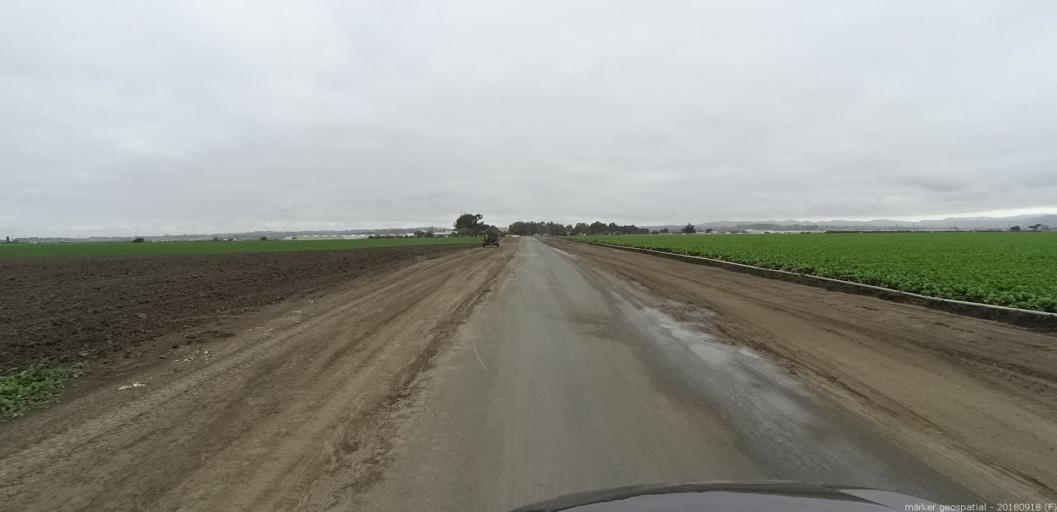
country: US
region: California
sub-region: Monterey County
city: Prunedale
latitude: 36.7395
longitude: -121.6935
